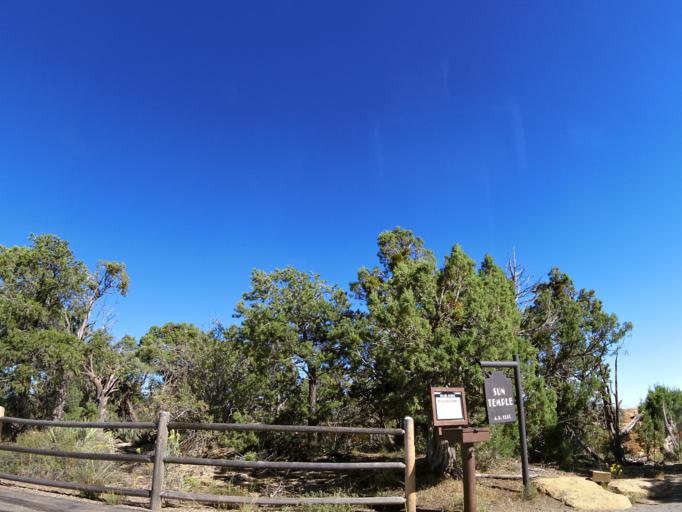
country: US
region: Colorado
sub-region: Montezuma County
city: Cortez
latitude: 37.1649
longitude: -108.4758
